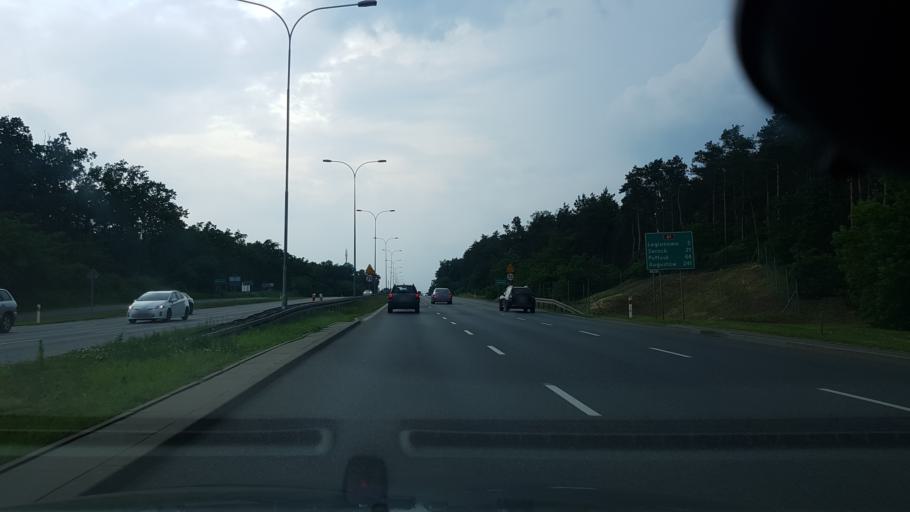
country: PL
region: Masovian Voivodeship
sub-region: Powiat legionowski
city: Jablonna
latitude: 52.3579
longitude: 20.9397
